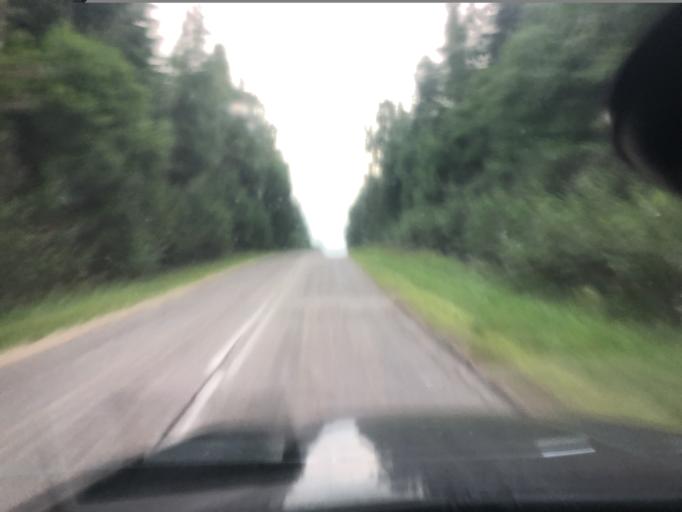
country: RU
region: Jaroslavl
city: Petrovsk
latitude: 56.9981
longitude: 39.0986
